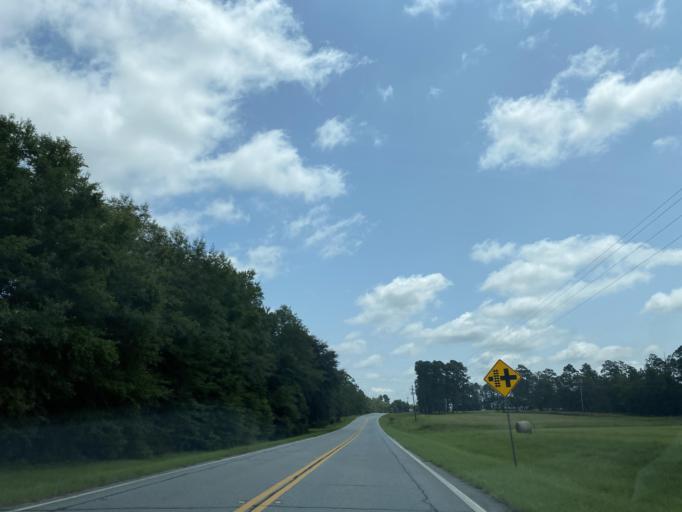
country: US
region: Georgia
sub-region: Wilcox County
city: Abbeville
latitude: 32.0077
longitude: -83.1232
